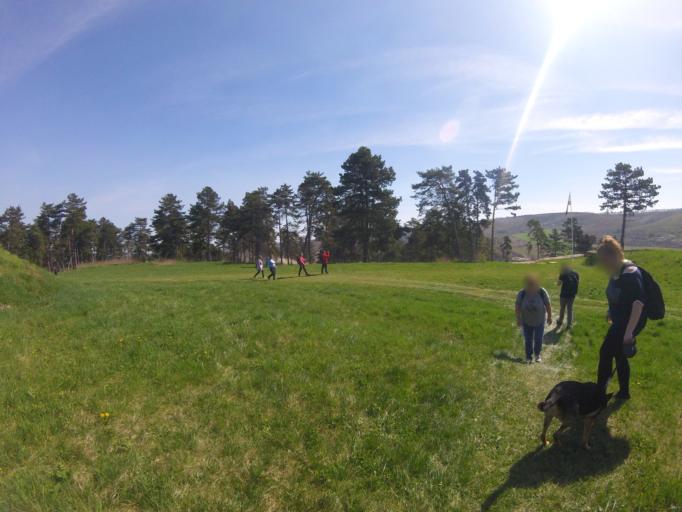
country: HU
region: Borsod-Abauj-Zemplen
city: Szendro
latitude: 48.4076
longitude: 20.7350
